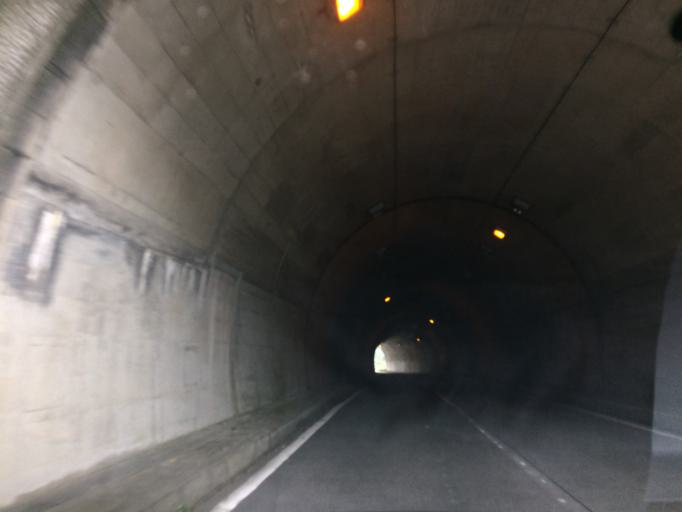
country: JP
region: Shizuoka
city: Shizuoka-shi
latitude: 35.1660
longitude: 138.1621
